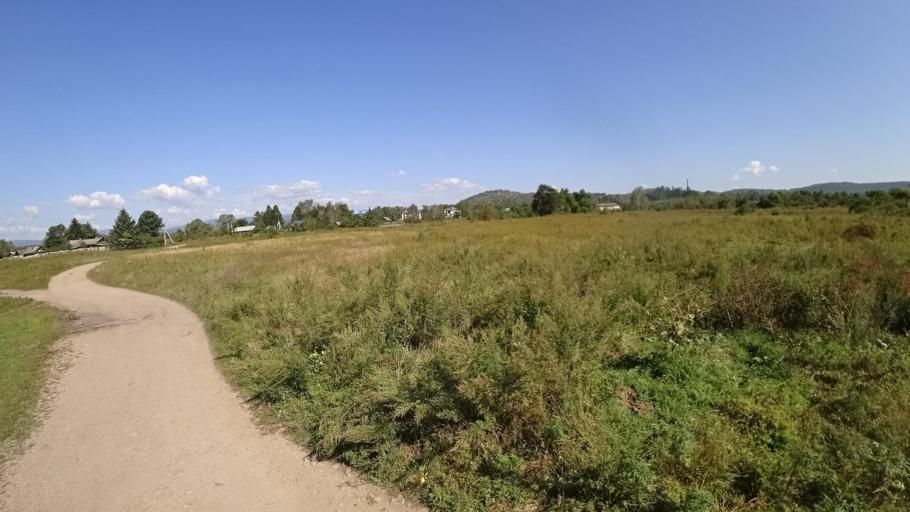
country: RU
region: Jewish Autonomous Oblast
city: Bira
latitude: 48.9936
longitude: 132.4550
